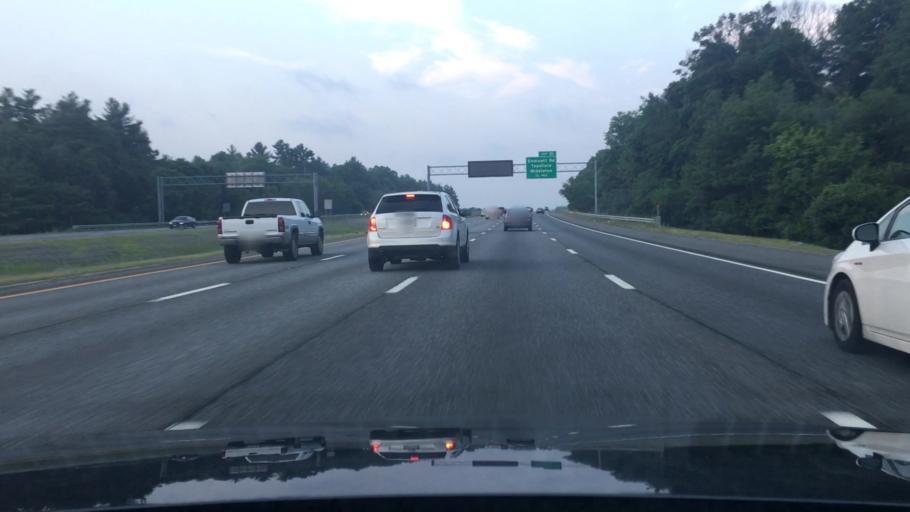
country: US
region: Massachusetts
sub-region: Essex County
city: Topsfield
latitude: 42.6365
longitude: -70.9773
